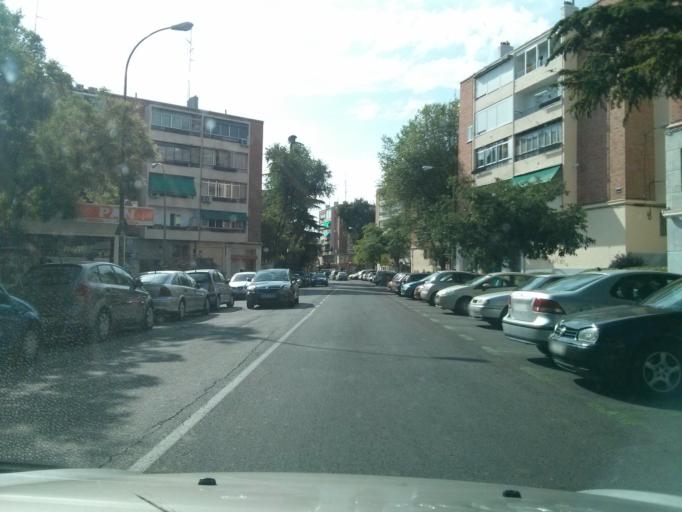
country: ES
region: Madrid
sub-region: Provincia de Madrid
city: Tetuan de las Victorias
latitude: 40.4727
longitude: -3.7108
